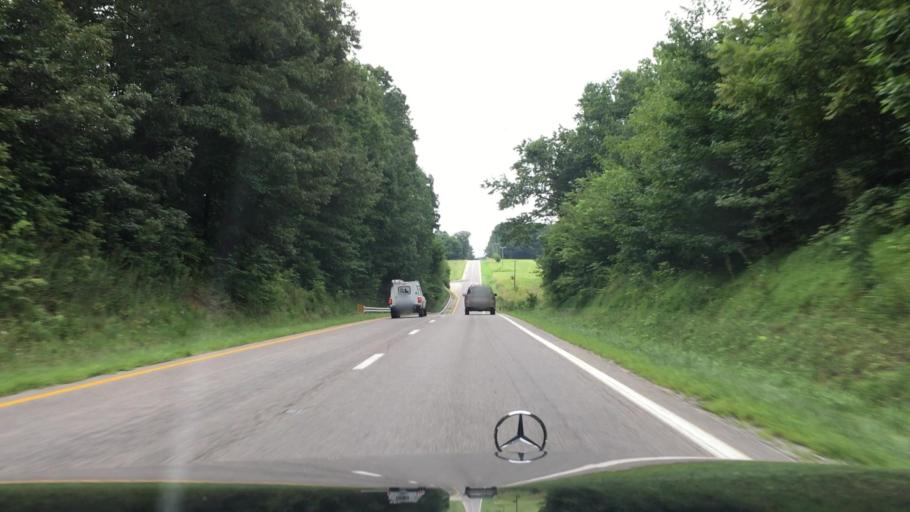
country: US
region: Virginia
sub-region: Prince Edward County
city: Hampden Sydney
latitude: 37.3059
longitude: -78.5193
